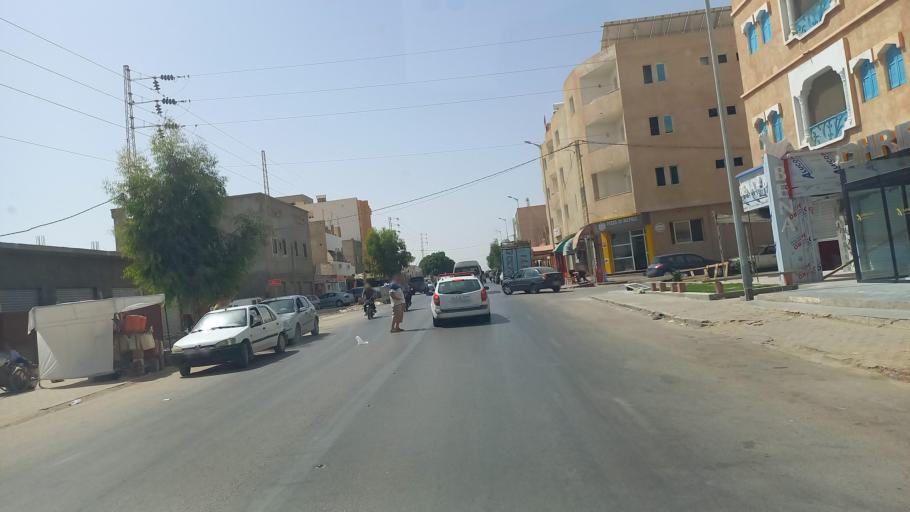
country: TN
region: Madanin
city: Medenine
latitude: 33.3286
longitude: 10.4849
